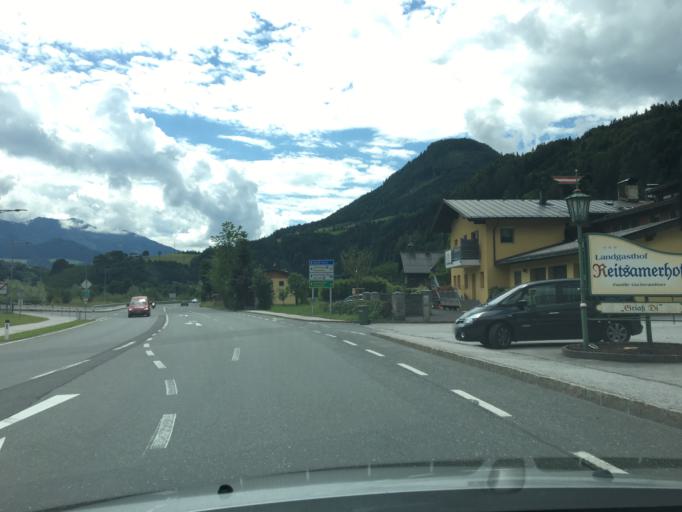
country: AT
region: Salzburg
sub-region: Politischer Bezirk Sankt Johann im Pongau
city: Pfarrwerfen
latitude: 47.4621
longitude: 13.1980
